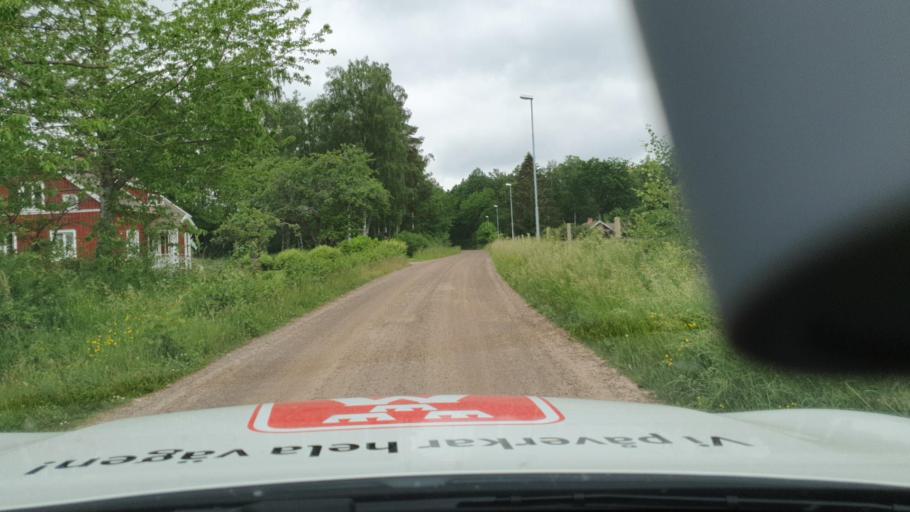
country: SE
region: Vaestra Goetaland
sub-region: Hjo Kommun
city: Hjo
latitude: 58.3529
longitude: 14.3429
